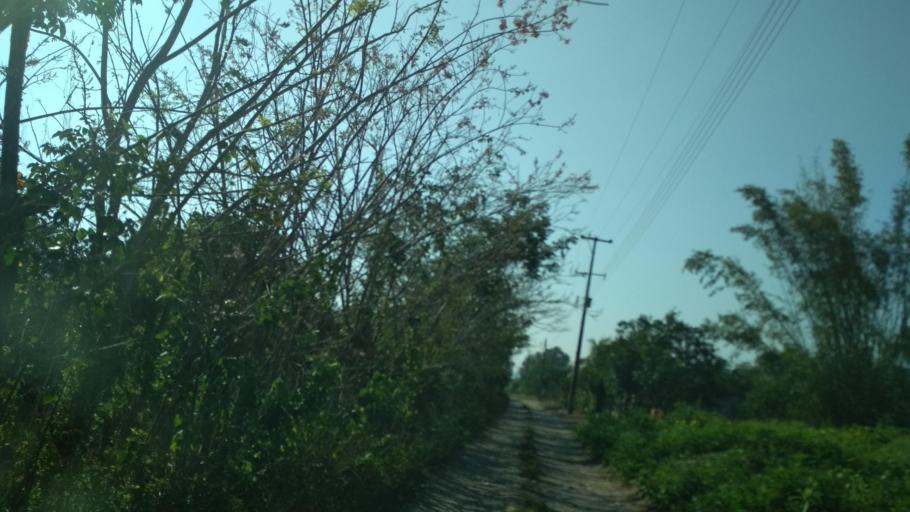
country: MX
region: Veracruz
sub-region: Papantla
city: Polutla
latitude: 20.4607
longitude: -97.2084
